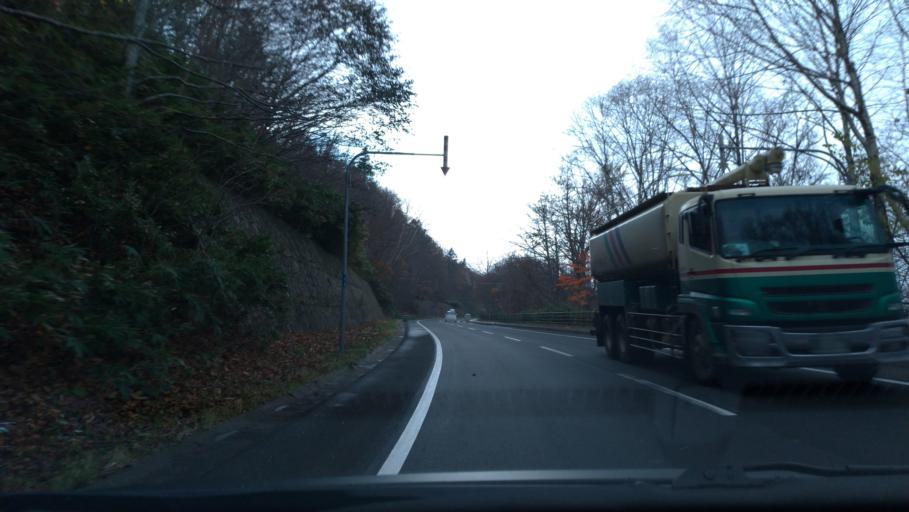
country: JP
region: Hokkaido
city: Shiraoi
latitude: 42.7359
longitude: 141.3516
